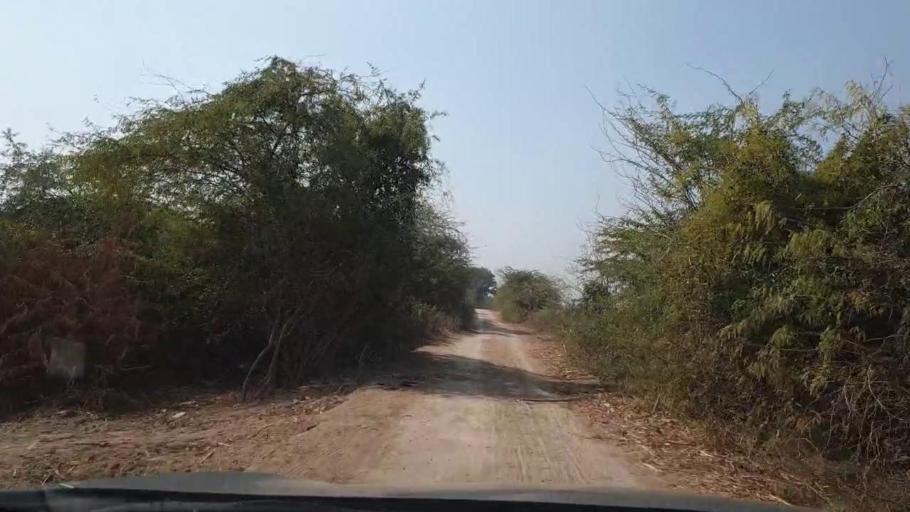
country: PK
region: Sindh
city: Tando Allahyar
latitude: 25.5057
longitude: 68.7918
